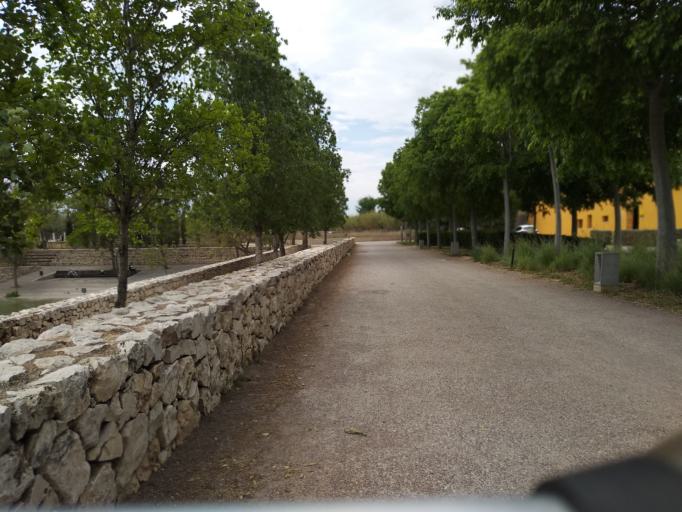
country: ES
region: Valencia
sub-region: Provincia de Valencia
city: Mislata
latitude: 39.4809
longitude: -0.4096
